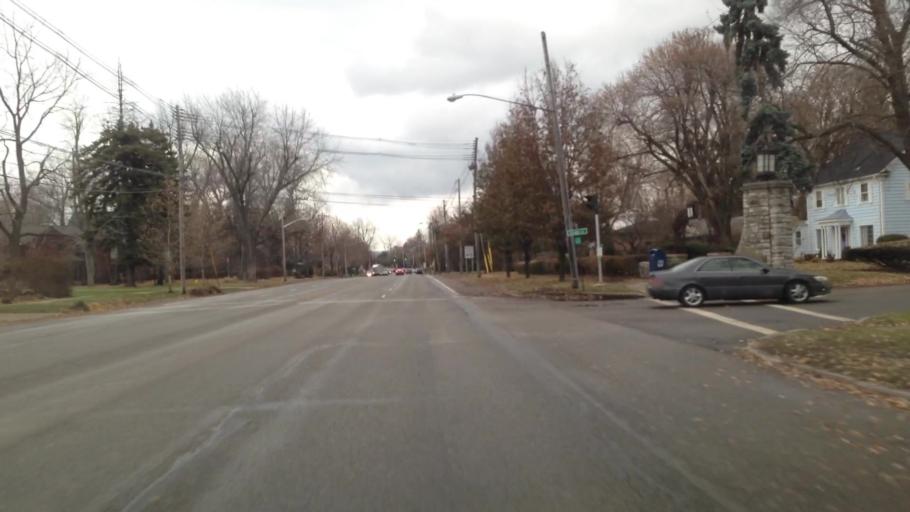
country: US
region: New York
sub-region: Erie County
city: Eggertsville
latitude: 42.9617
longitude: -78.7786
